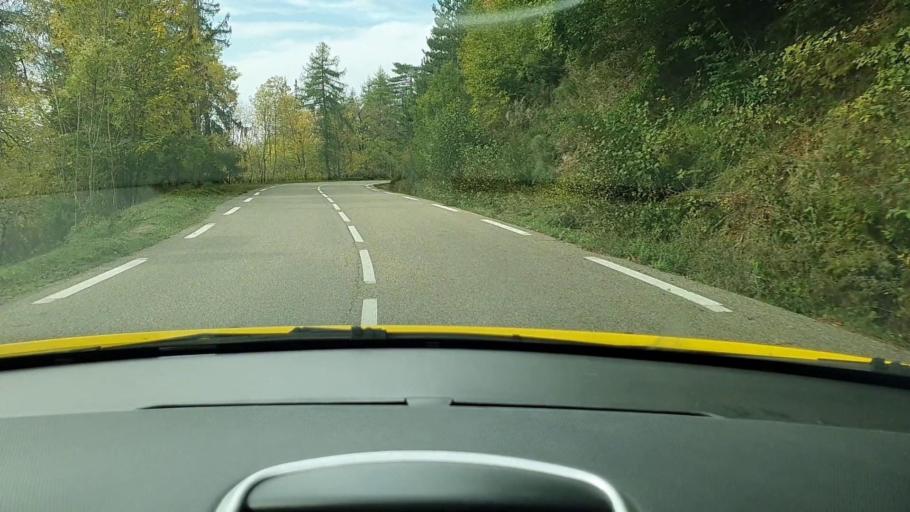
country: FR
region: Languedoc-Roussillon
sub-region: Departement de la Lozere
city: Meyrueis
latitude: 44.1249
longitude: 3.4546
